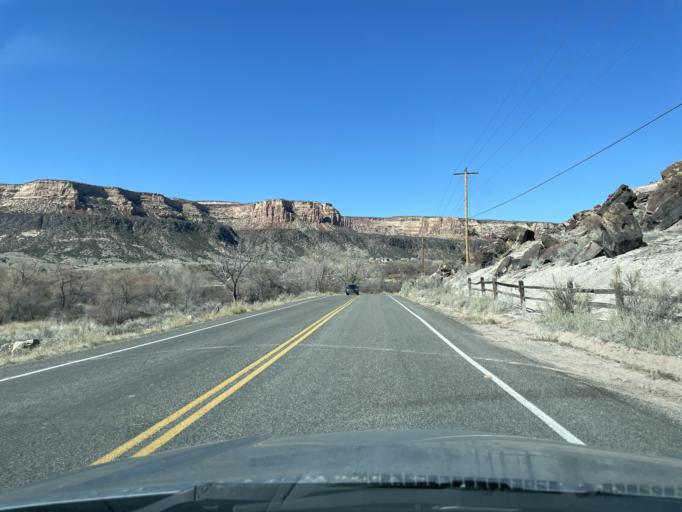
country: US
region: Colorado
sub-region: Mesa County
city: Redlands
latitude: 39.0728
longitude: -108.6510
